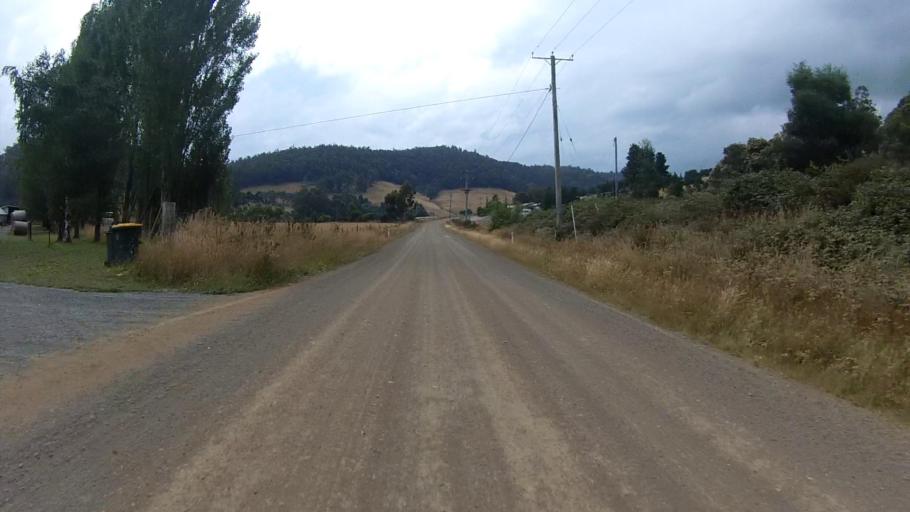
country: AU
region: Tasmania
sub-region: Huon Valley
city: Huonville
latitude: -42.9767
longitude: 147.0549
